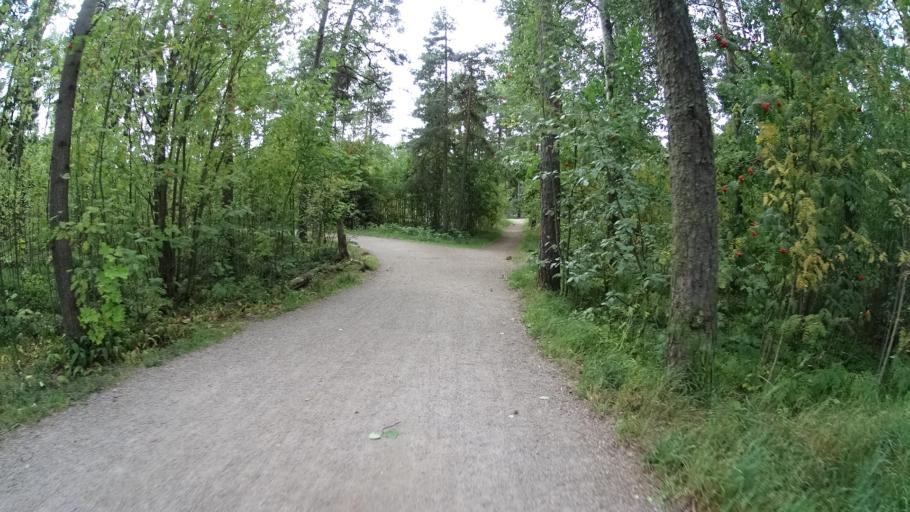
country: FI
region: Uusimaa
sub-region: Helsinki
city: Helsinki
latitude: 60.1953
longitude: 24.9093
